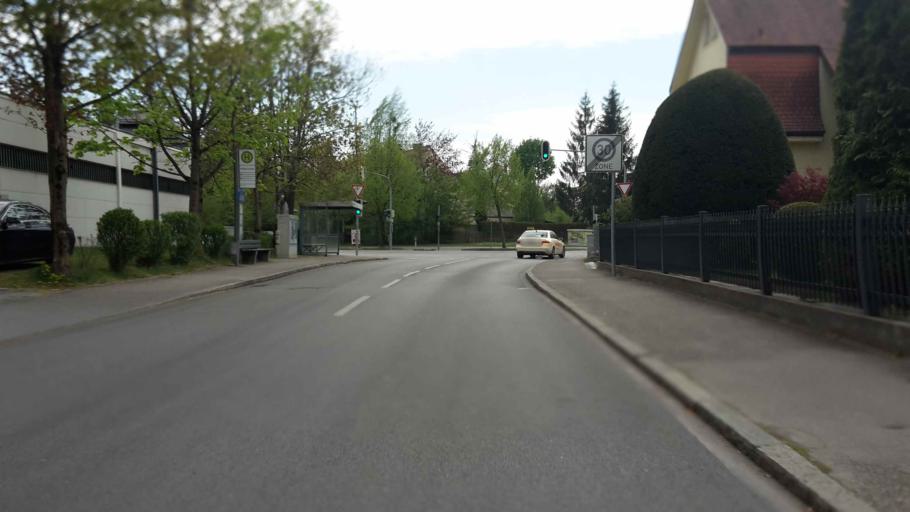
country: DE
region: Bavaria
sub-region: Upper Bavaria
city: Karlsfeld
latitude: 48.1799
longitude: 11.4897
